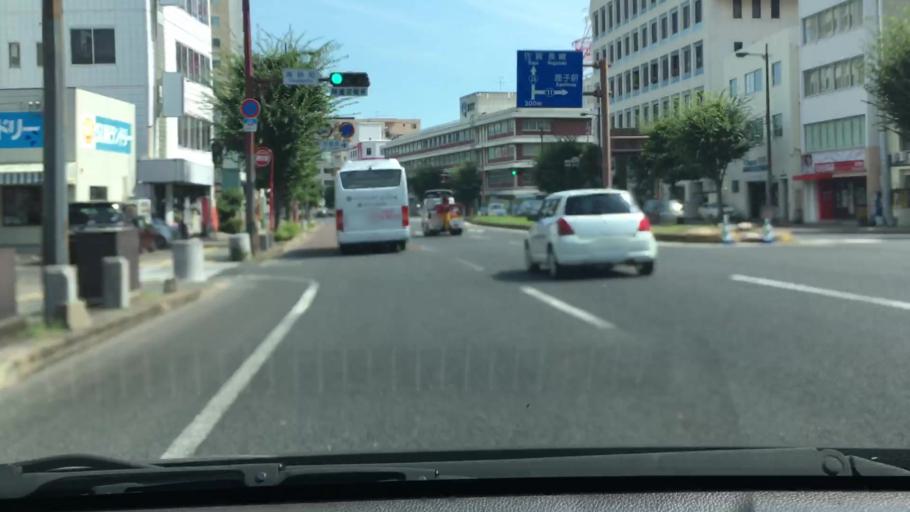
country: JP
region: Nagasaki
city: Sasebo
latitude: 33.1786
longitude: 129.7163
